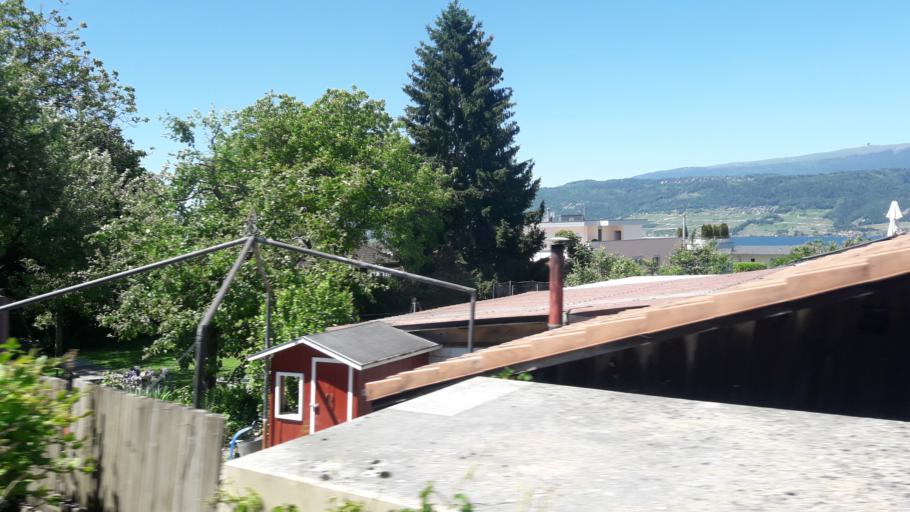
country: CH
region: Bern
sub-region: Seeland District
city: Tauffelen
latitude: 47.0737
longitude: 7.2008
